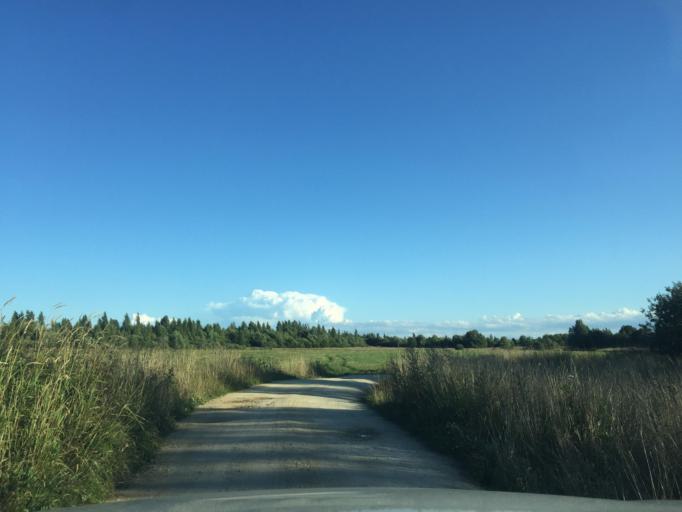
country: RU
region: Leningrad
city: Rozhdestveno
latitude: 59.3294
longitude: 29.9984
